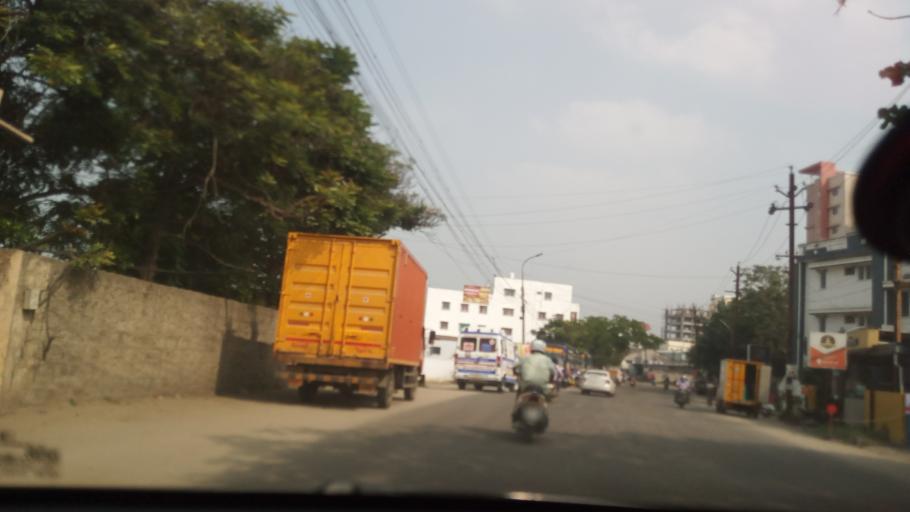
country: IN
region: Tamil Nadu
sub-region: Coimbatore
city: Coimbatore
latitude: 11.0213
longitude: 76.9884
